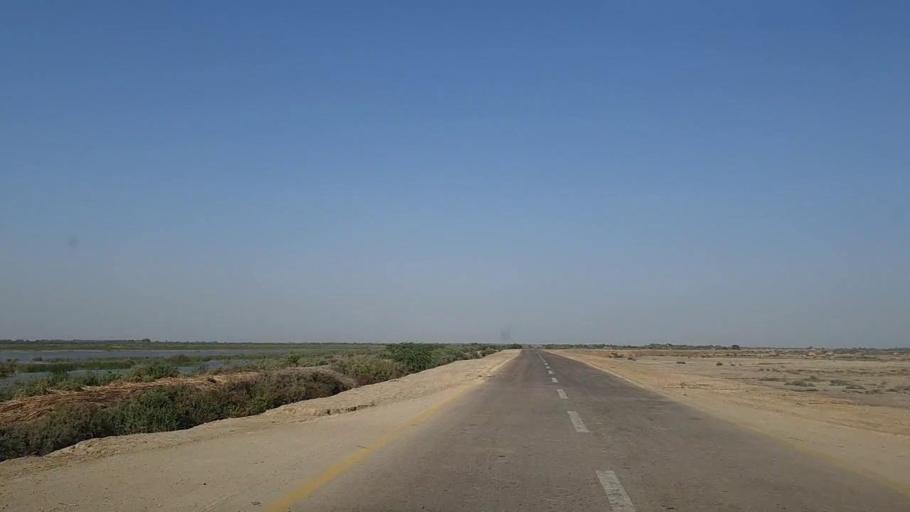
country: PK
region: Sindh
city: Jati
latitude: 24.4389
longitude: 68.3184
